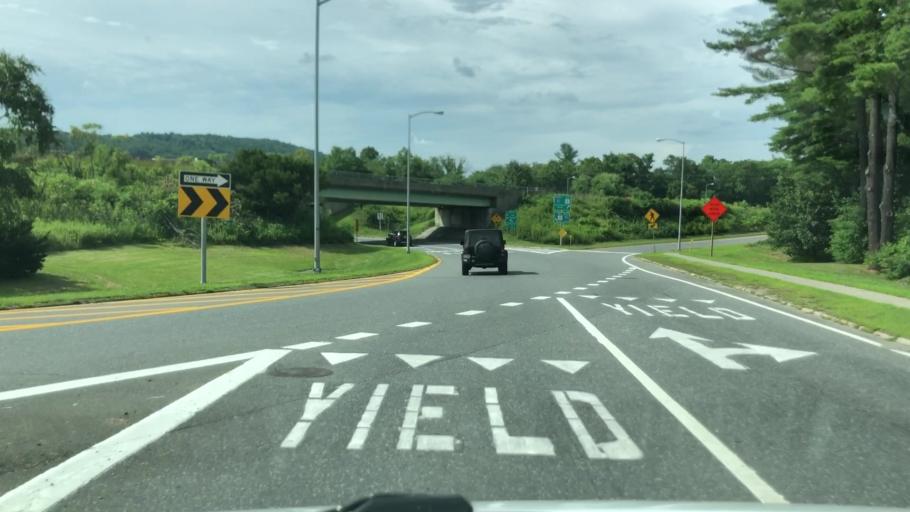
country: US
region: Massachusetts
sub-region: Franklin County
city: Greenfield
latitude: 42.5853
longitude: -72.6203
